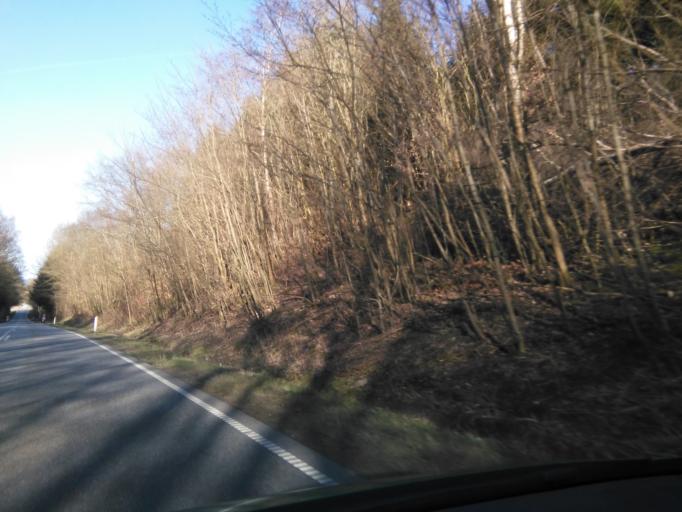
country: DK
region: Central Jutland
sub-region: Skanderborg Kommune
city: Ry
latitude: 56.0119
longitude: 9.7947
